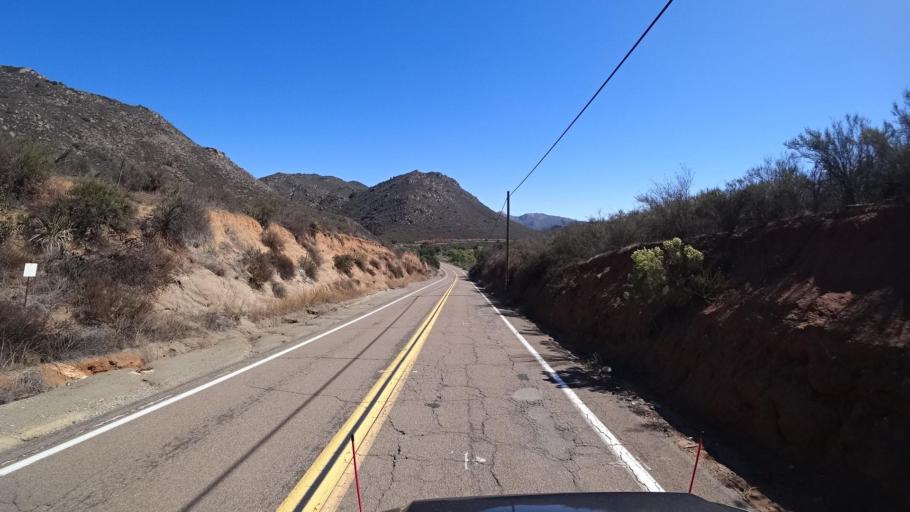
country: US
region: California
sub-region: San Diego County
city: Alpine
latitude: 32.7990
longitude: -116.7547
